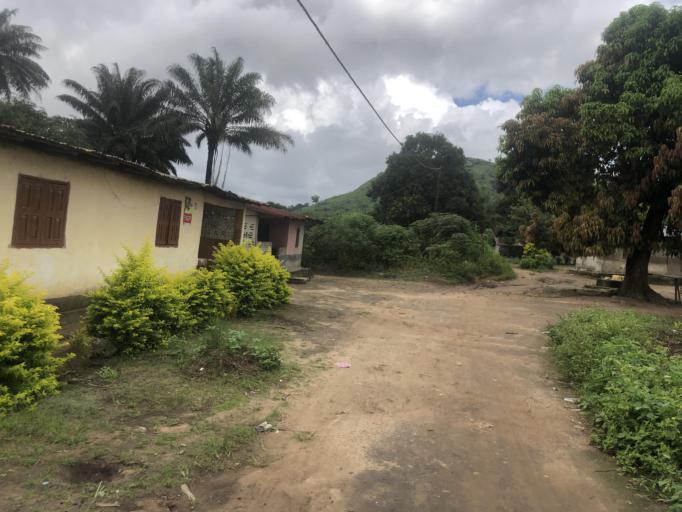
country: SL
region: Northern Province
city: Makeni
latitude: 8.9065
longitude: -12.0398
